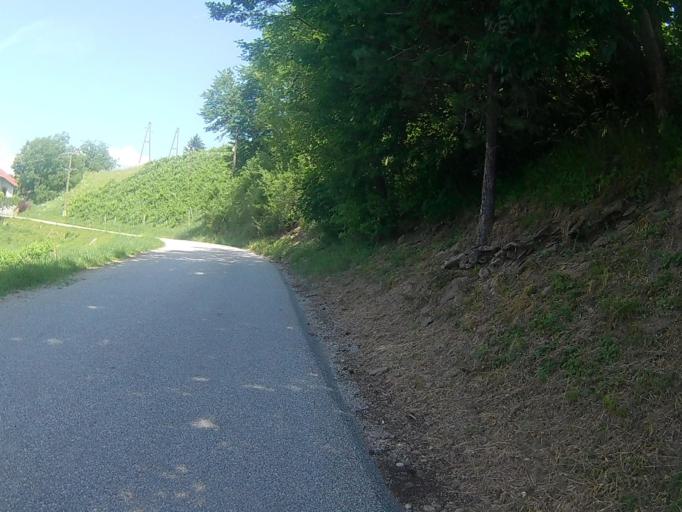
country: SI
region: Maribor
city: Kamnica
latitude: 46.6058
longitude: 15.6043
